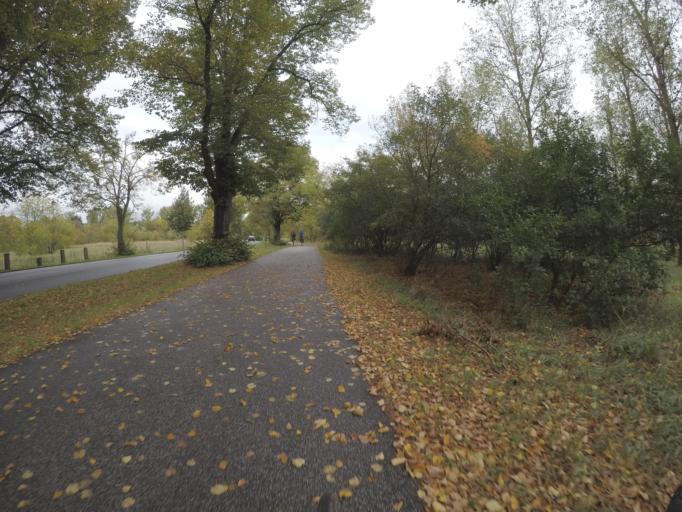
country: DE
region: Berlin
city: Buch
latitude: 52.6608
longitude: 13.4921
